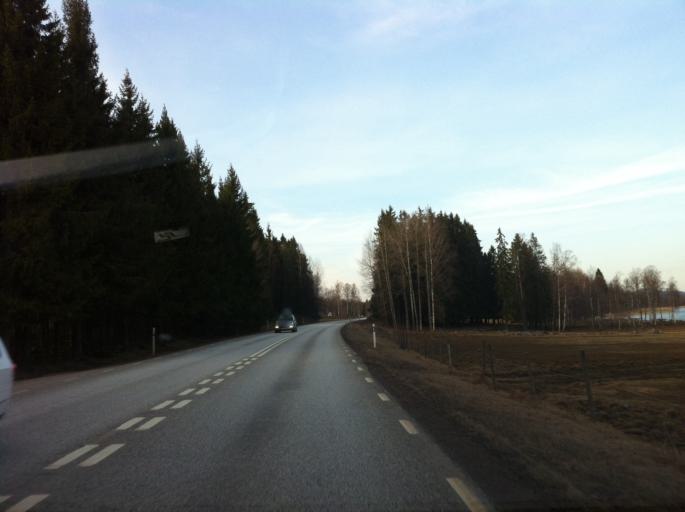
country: SE
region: Vaermland
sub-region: Storfors Kommun
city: Storfors
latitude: 59.5750
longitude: 14.2584
